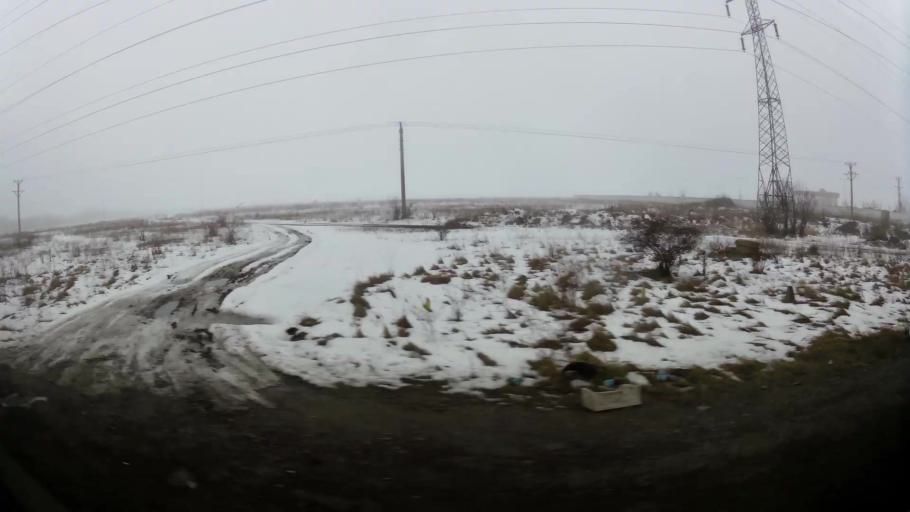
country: RO
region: Ilfov
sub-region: Comuna Clinceni
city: Olteni
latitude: 44.4239
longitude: 25.9678
